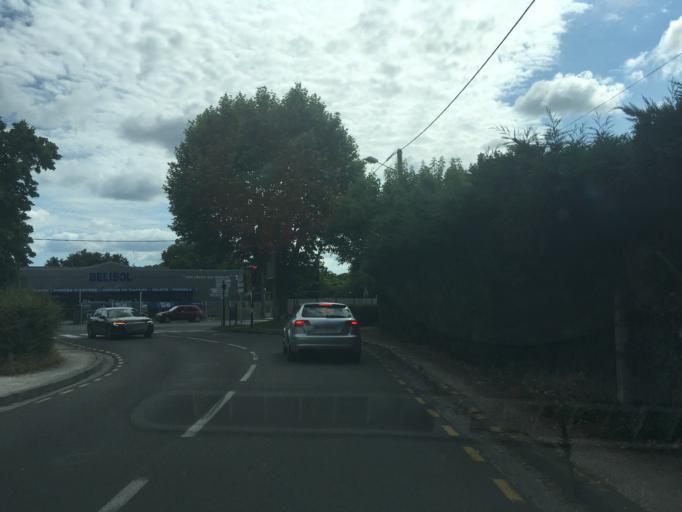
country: FR
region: Aquitaine
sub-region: Departement de la Gironde
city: Eysines
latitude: 44.8637
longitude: -0.6568
